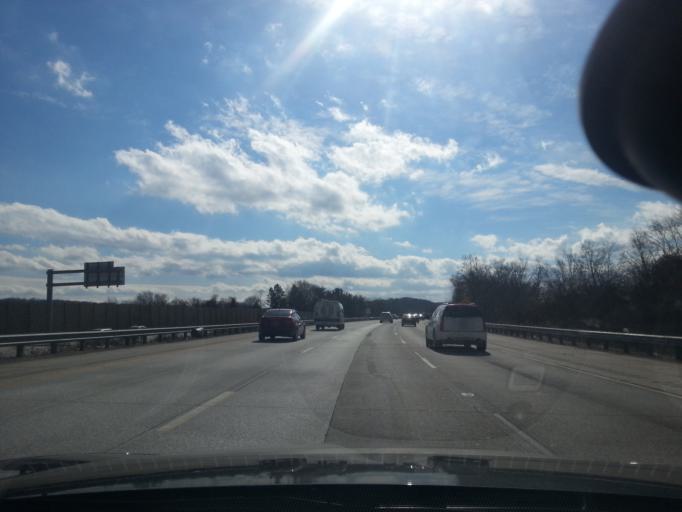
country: US
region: Pennsylvania
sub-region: Montgomery County
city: Conshohocken
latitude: 40.0825
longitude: -75.3122
